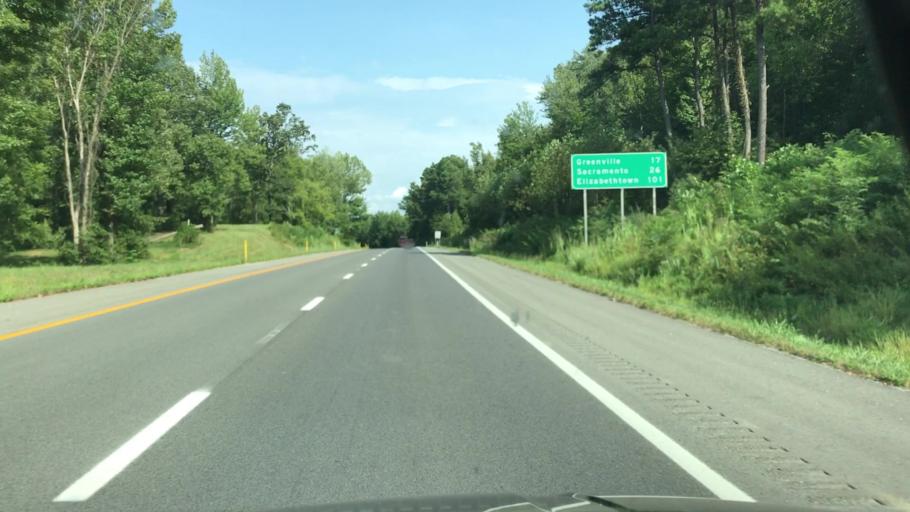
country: US
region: Kentucky
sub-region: Hopkins County
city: Nortonville
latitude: 37.2116
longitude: -87.4251
